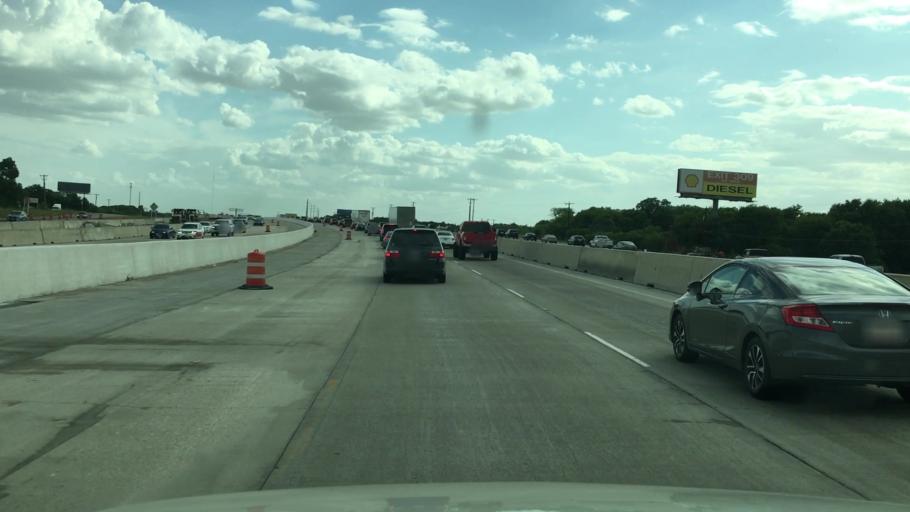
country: US
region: Texas
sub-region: McLennan County
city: Bruceville-Eddy
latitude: 31.3185
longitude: -97.2377
